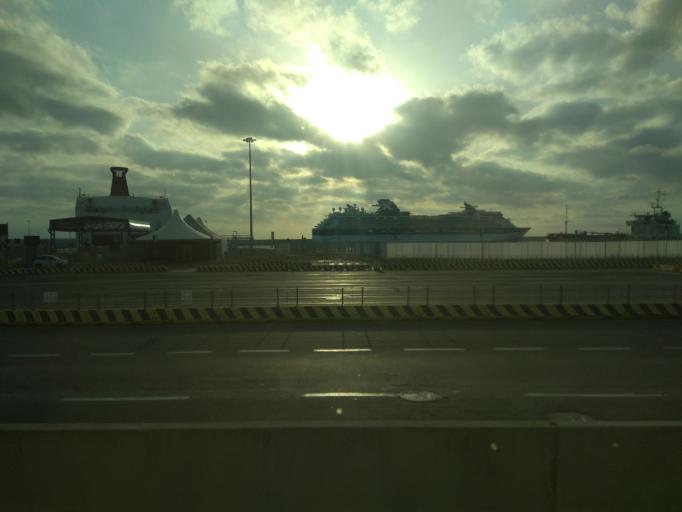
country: IT
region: Latium
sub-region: Citta metropolitana di Roma Capitale
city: Civitavecchia
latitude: 42.1002
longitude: 11.7839
